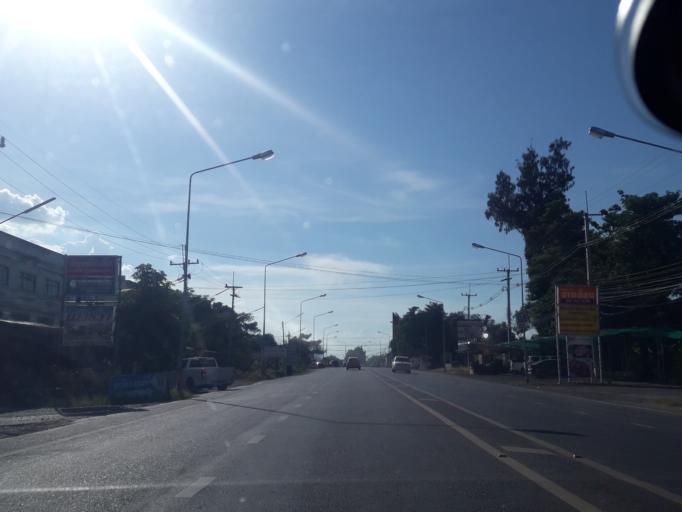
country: TH
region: Sara Buri
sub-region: Amphoe Wang Muang
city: Wang Muang
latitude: 14.8629
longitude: 101.0590
